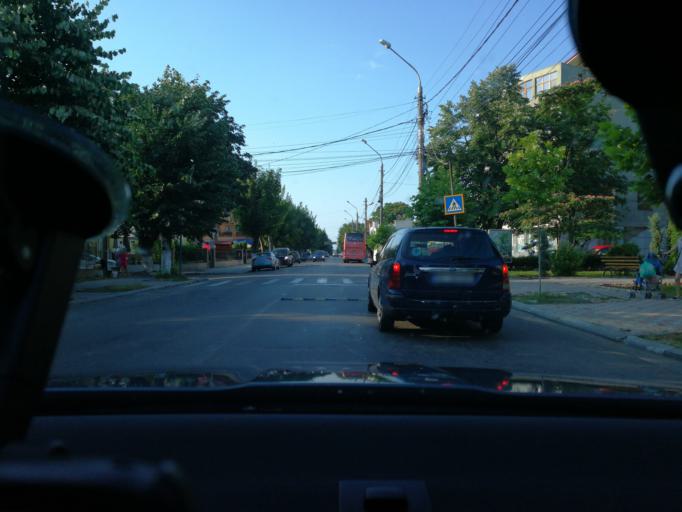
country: RO
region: Constanta
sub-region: Oras Eforie
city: Eforie Nord
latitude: 44.0672
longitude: 28.6331
